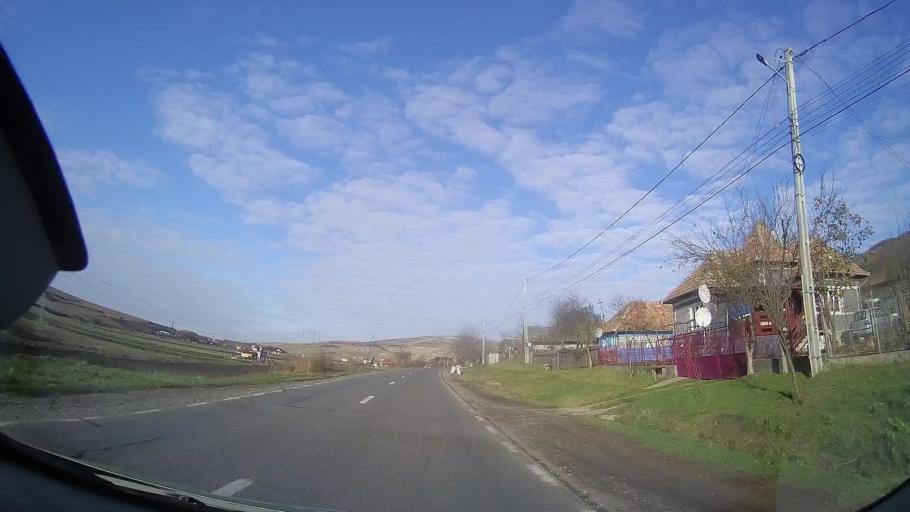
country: RO
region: Cluj
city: Caianu Mic
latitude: 46.8029
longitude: 23.8738
